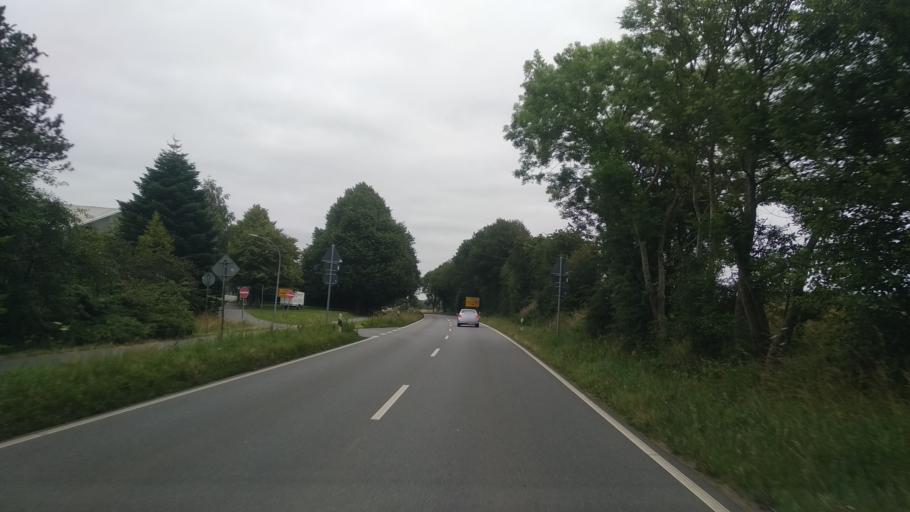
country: DE
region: Schleswig-Holstein
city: Langballig
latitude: 54.7978
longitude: 9.6306
